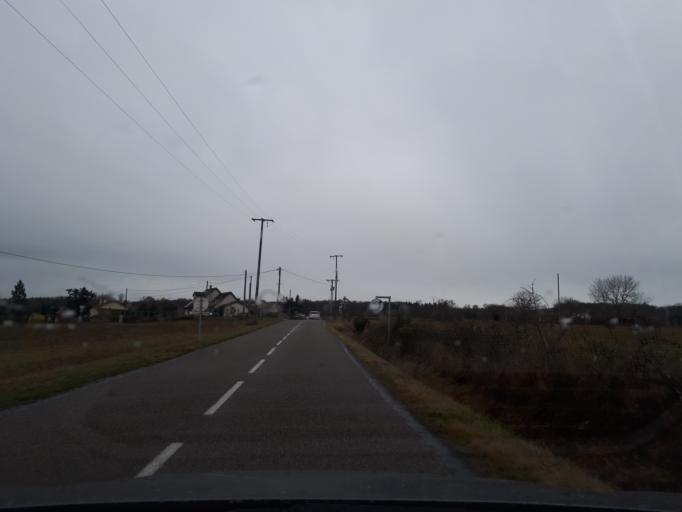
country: FR
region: Rhone-Alpes
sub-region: Departement de la Loire
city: Boen-sur-Lignon
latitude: 45.7710
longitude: 4.0055
